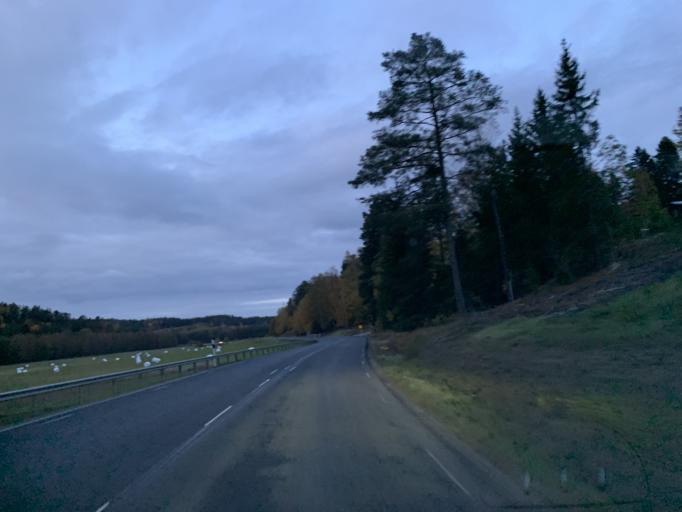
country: SE
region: Stockholm
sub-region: Botkyrka Kommun
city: Varsta
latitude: 59.1101
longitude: 17.8048
